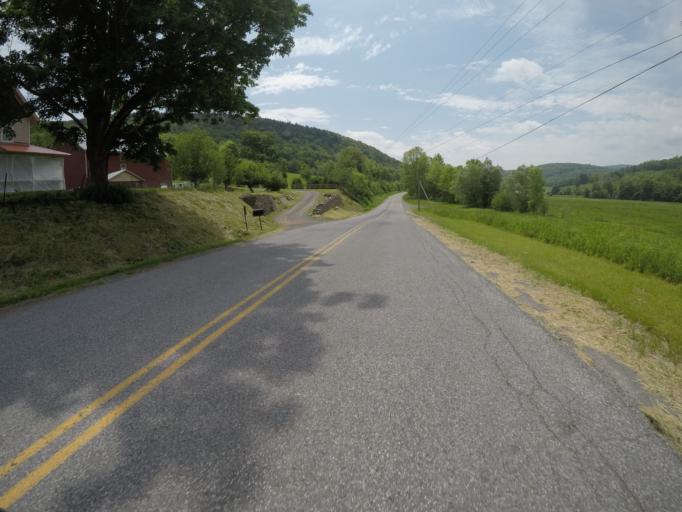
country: US
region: New York
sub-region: Delaware County
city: Stamford
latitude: 42.1753
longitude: -74.6738
